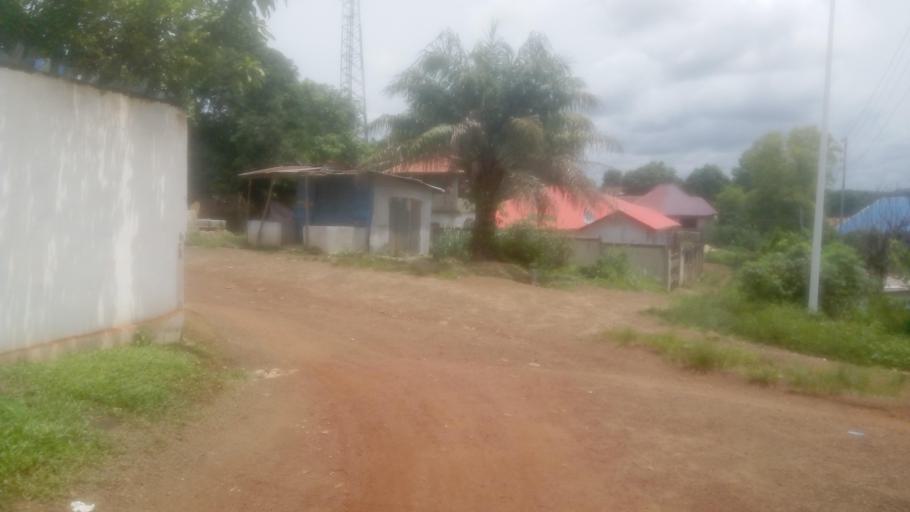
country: SL
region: Southern Province
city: Bo
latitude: 7.9556
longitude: -11.7123
